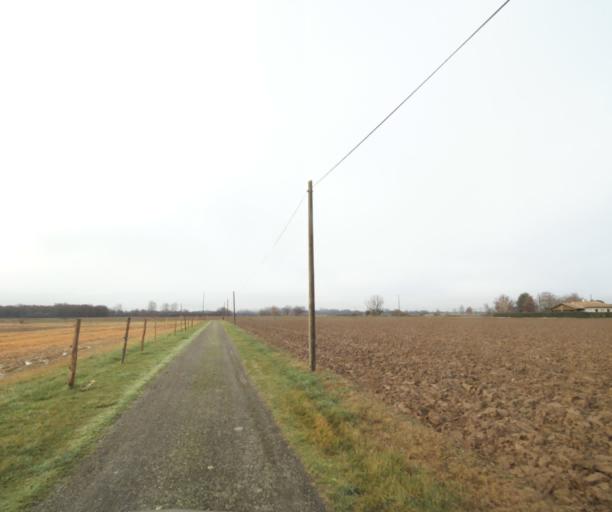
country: FR
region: Midi-Pyrenees
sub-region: Departement de la Haute-Garonne
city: Villemur-sur-Tarn
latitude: 43.8867
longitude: 1.4799
